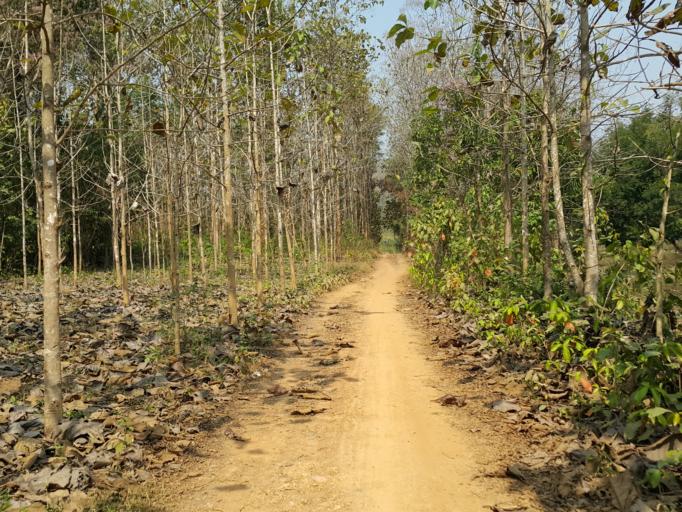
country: TH
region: Sukhothai
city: Thung Saliam
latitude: 17.3167
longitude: 99.5007
